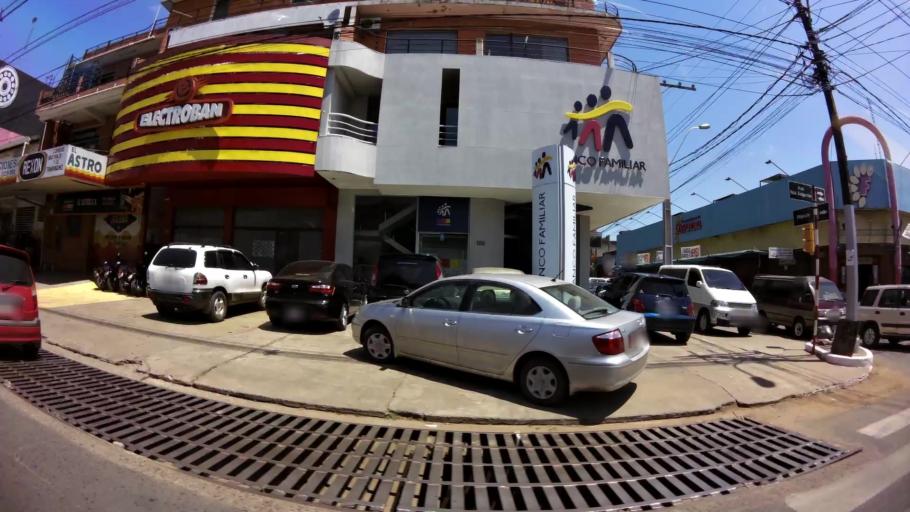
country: PY
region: Central
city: Fernando de la Mora
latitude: -25.3263
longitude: -57.5490
